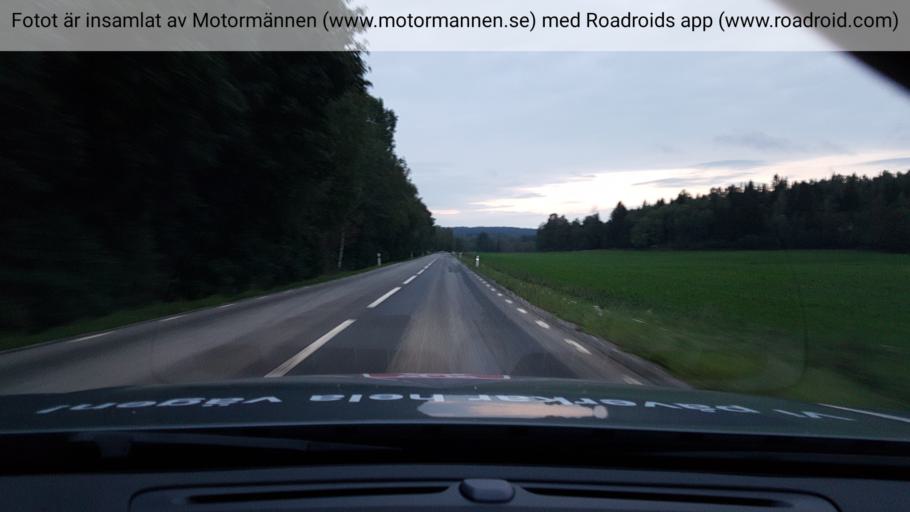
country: SE
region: OErebro
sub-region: Nora Kommun
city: As
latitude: 59.4543
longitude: 14.8793
